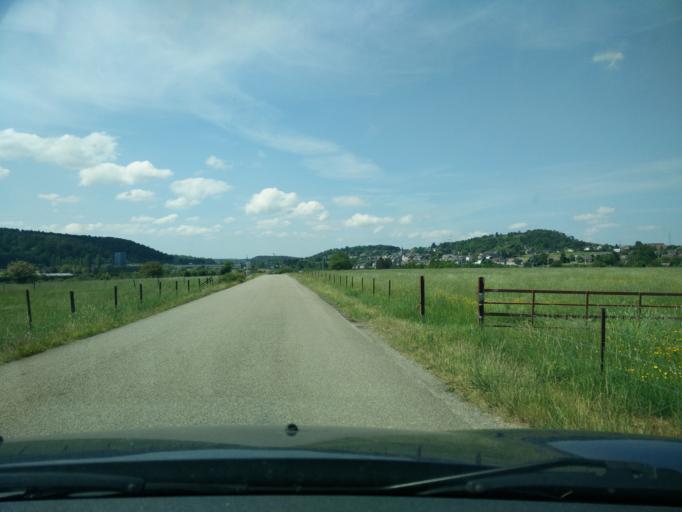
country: BE
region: Wallonia
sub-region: Province de Namur
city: Couvin
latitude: 50.0821
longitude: 4.5240
